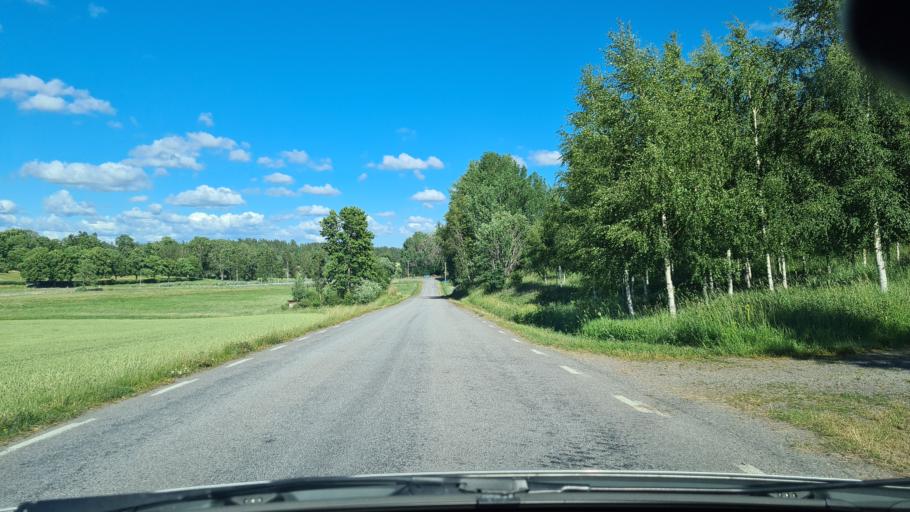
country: SE
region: Soedermanland
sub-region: Nykopings Kommun
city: Olstorp
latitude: 58.8285
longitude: 16.5152
